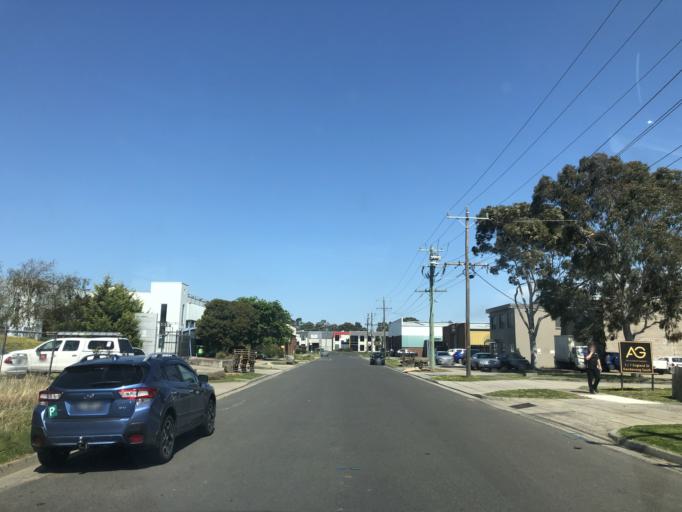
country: AU
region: Victoria
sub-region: Casey
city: Hampton Park
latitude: -38.0308
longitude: 145.2190
